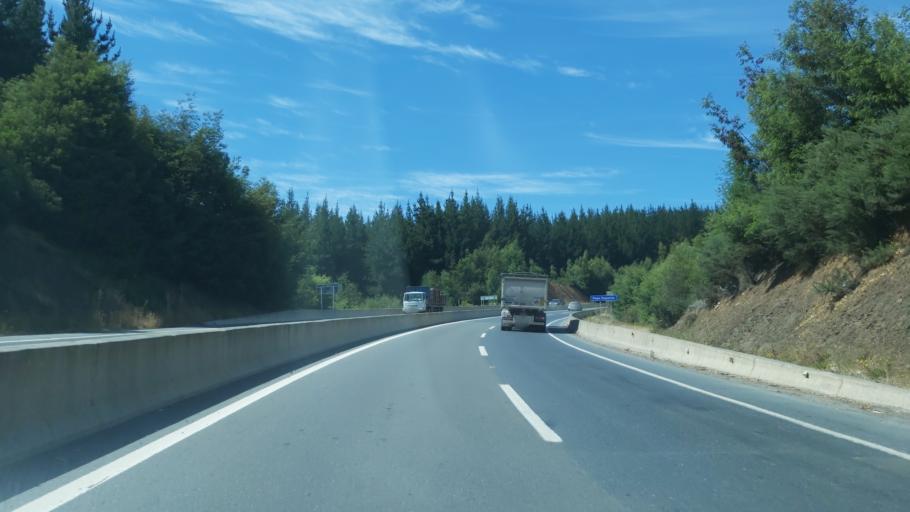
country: CL
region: Biobio
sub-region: Provincia de Concepcion
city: Lota
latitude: -37.0801
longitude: -73.1368
